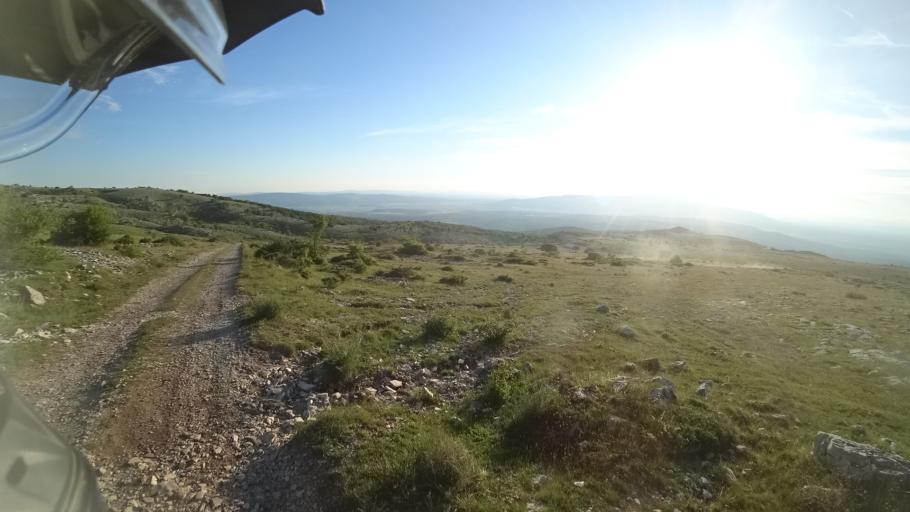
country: HR
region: Sibensko-Kniniska
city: Drnis
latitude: 43.8846
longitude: 16.3360
